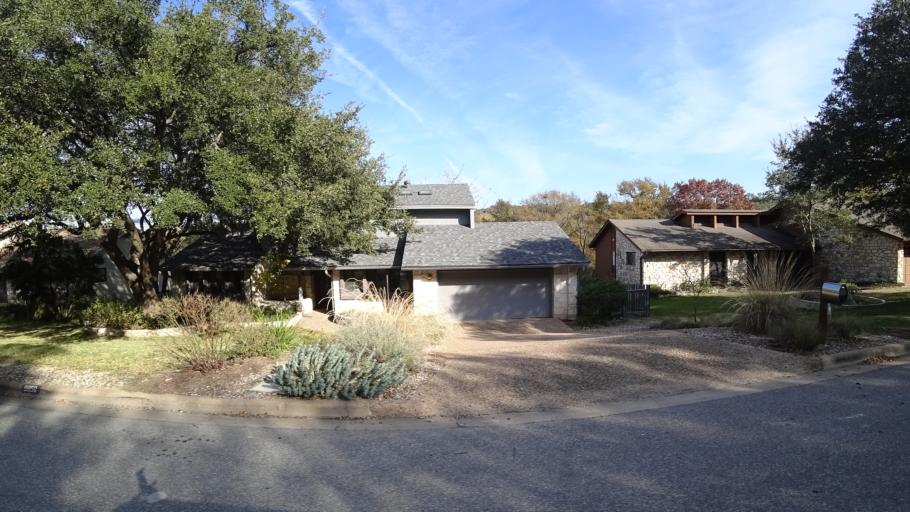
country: US
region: Texas
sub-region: Williamson County
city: Jollyville
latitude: 30.3853
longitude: -97.7531
